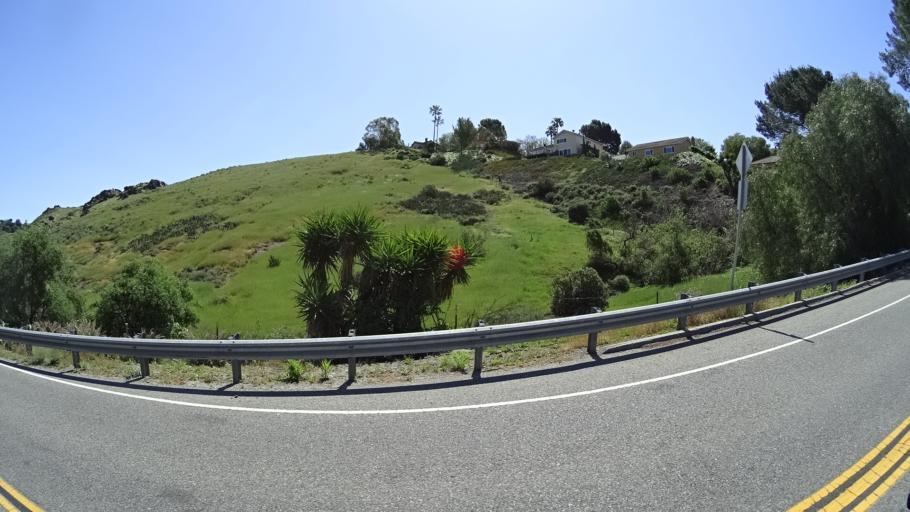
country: US
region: California
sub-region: Ventura County
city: Moorpark
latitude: 34.2346
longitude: -118.8647
